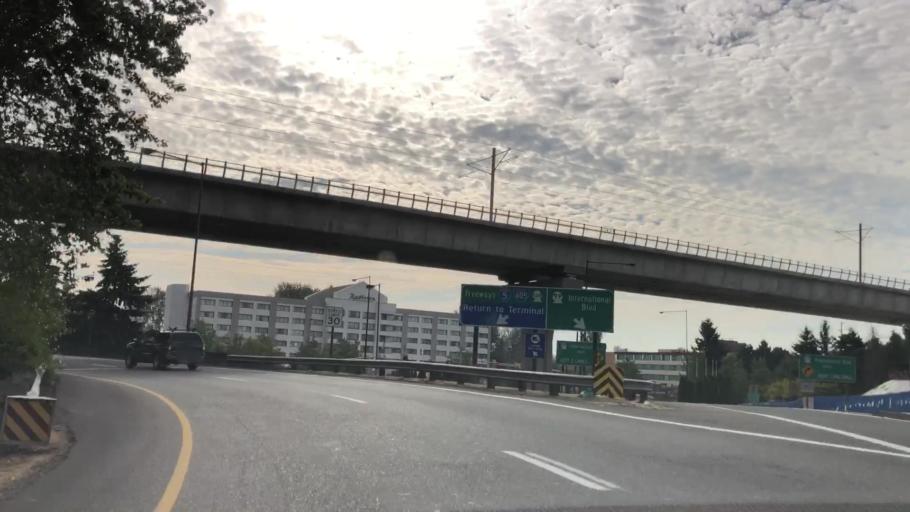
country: US
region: Washington
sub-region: King County
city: SeaTac
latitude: 47.4401
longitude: -122.3004
